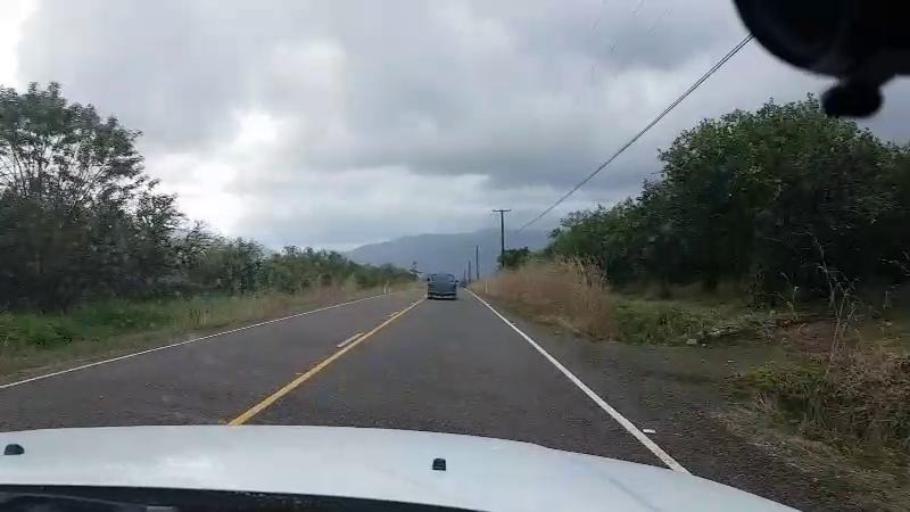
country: BZ
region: Cayo
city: Belmopan
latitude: 17.1252
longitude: -88.6513
